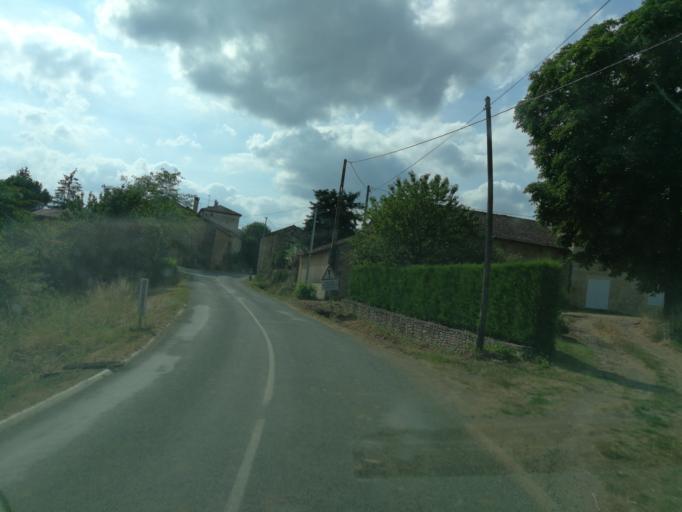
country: FR
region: Aquitaine
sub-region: Departement du Lot-et-Garonne
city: Monsempron-Libos
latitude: 44.5271
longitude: 0.9403
